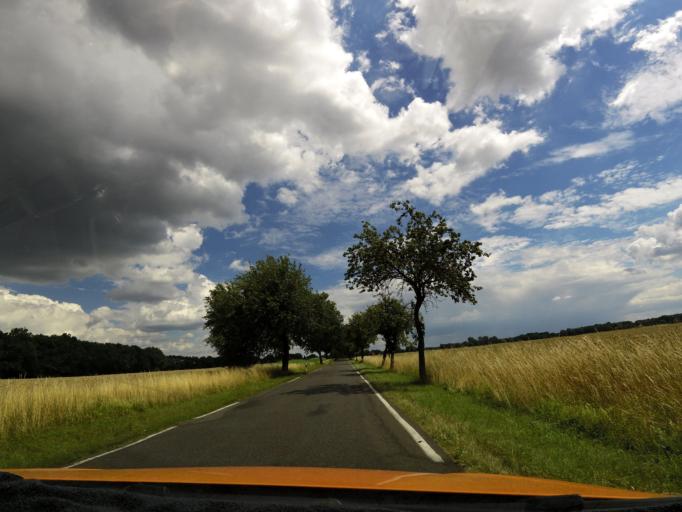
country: DE
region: Brandenburg
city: Storkow
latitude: 52.2475
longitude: 13.8838
